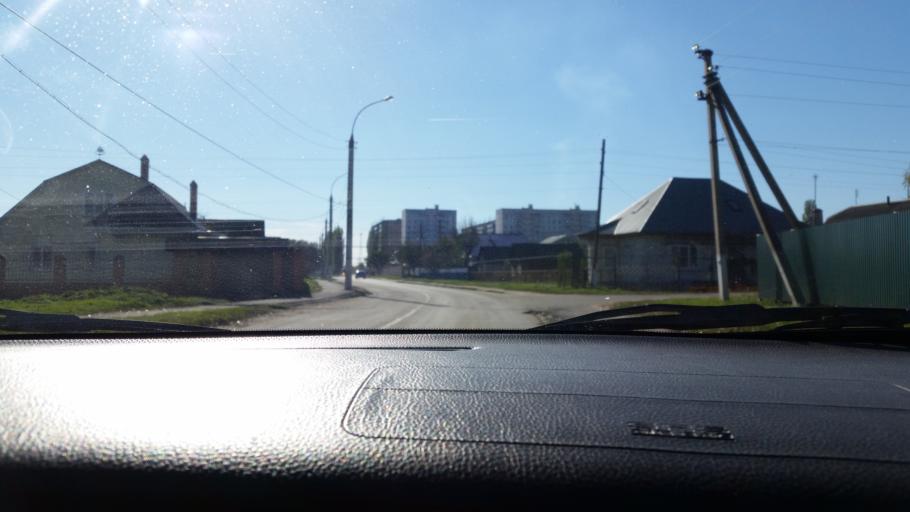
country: RU
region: Lipetsk
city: Gryazi
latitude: 52.4770
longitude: 39.9494
